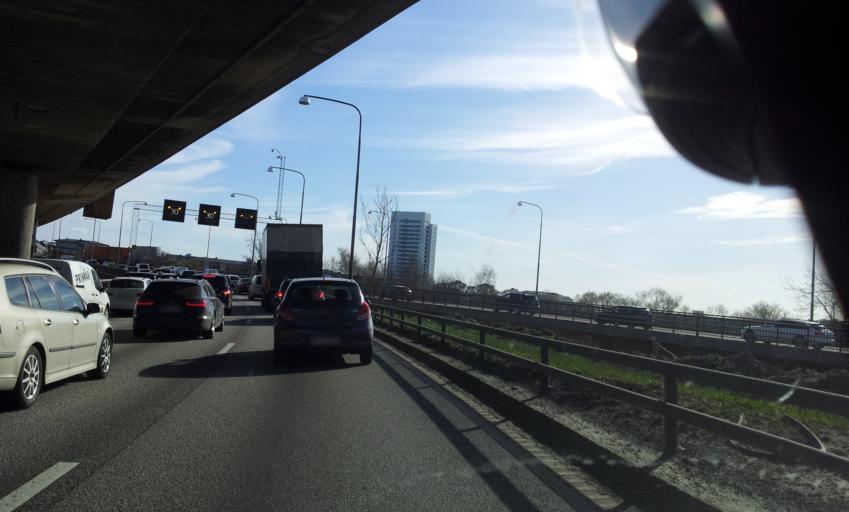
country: SE
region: Stockholm
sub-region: Solna Kommun
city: Solna
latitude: 59.3444
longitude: 18.0092
